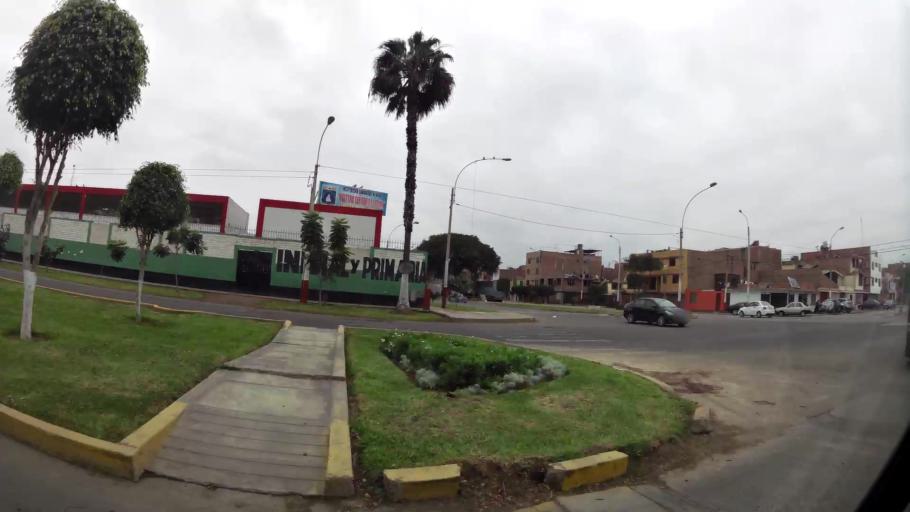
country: PE
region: Callao
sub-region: Callao
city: Callao
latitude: -12.0529
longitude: -77.1082
